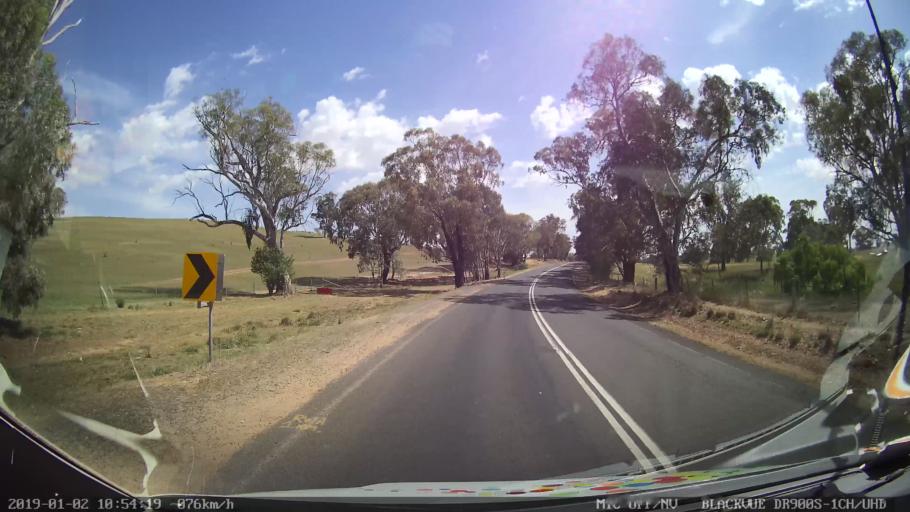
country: AU
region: New South Wales
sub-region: Cootamundra
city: Cootamundra
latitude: -34.6711
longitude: 148.2729
